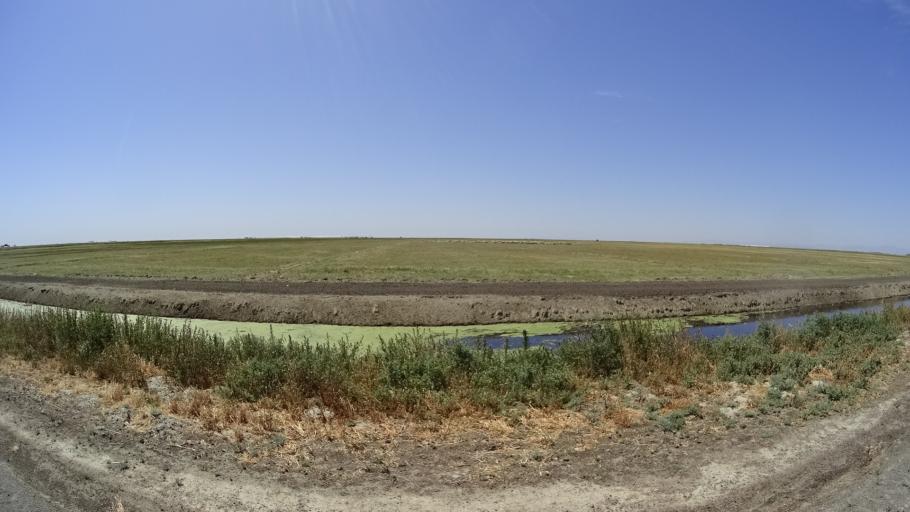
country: US
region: California
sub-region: Kings County
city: Stratford
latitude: 36.1893
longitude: -119.7027
